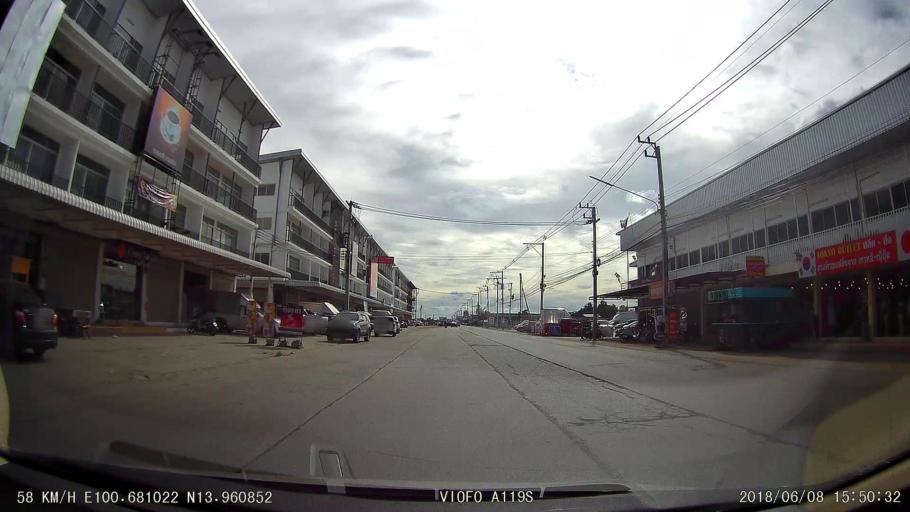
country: TH
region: Bangkok
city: Sai Mai
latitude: 13.9609
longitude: 100.6810
